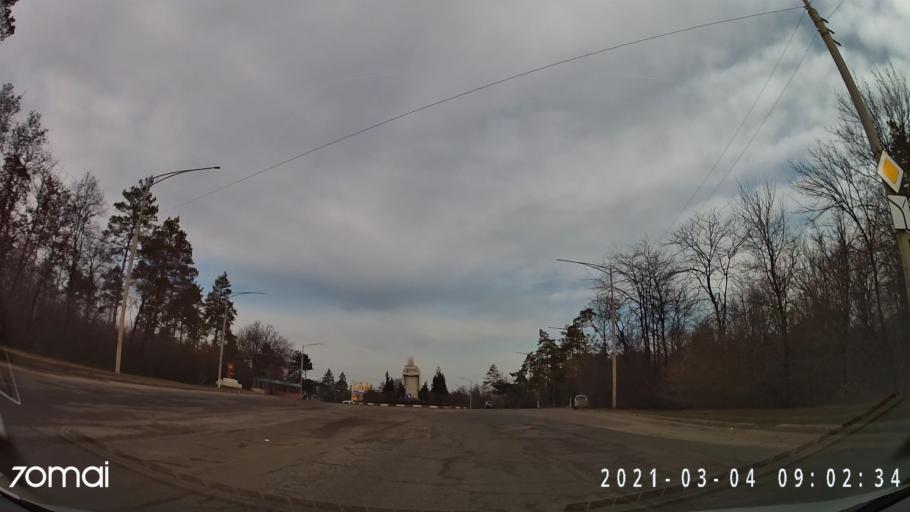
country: MD
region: Balti
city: Balti
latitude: 47.7441
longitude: 27.9535
